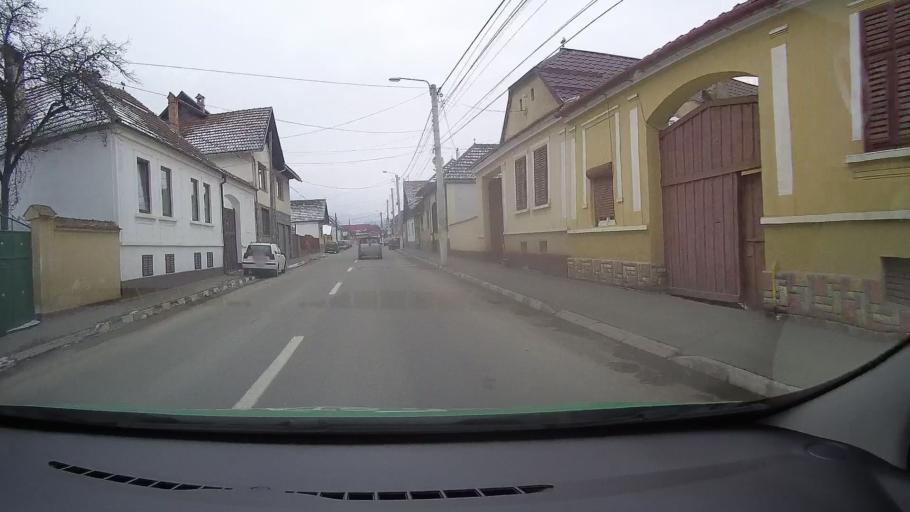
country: RO
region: Brasov
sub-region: Oras Rasnov
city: Rasnov
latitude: 45.5789
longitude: 25.4571
